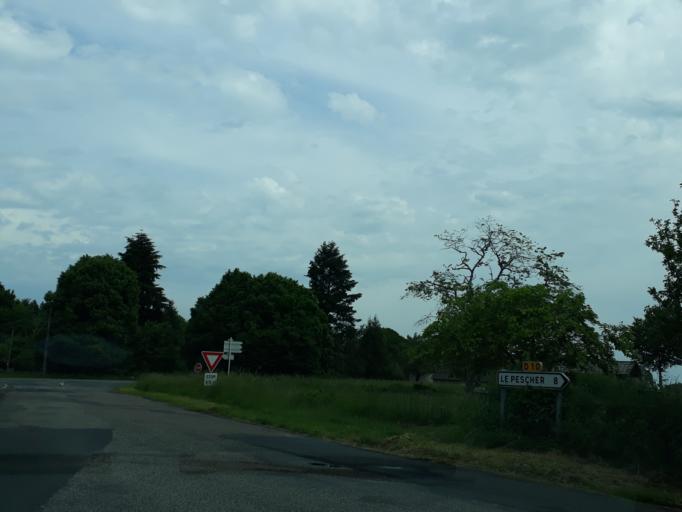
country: FR
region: Limousin
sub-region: Departement de la Correze
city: Beynat
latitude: 45.1050
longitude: 1.7765
